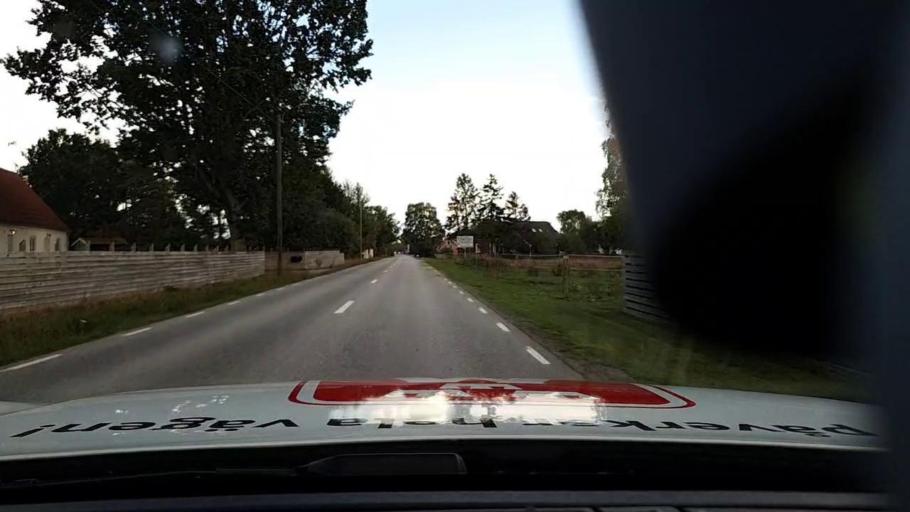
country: SE
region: Blekinge
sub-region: Solvesborgs Kommun
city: Soelvesborg
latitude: 56.0191
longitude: 14.7167
